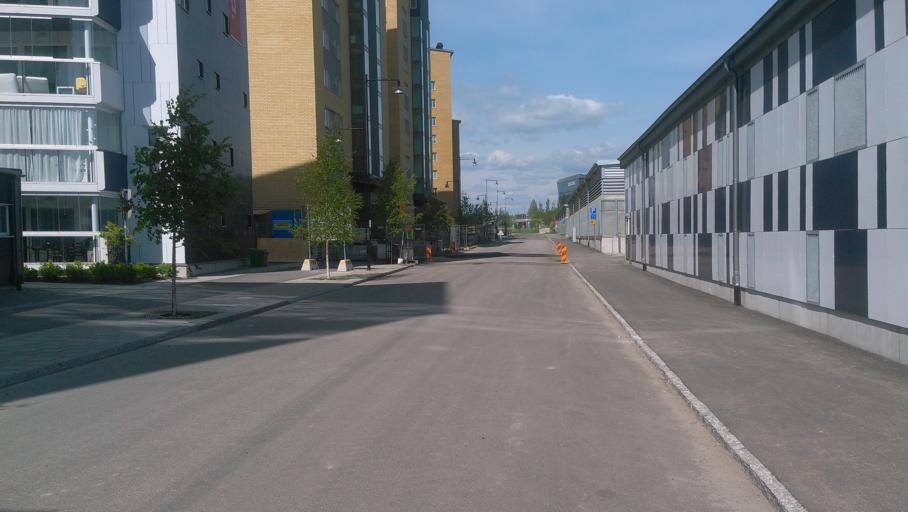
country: SE
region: Vaesterbotten
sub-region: Umea Kommun
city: Umea
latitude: 63.8150
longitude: 20.2935
